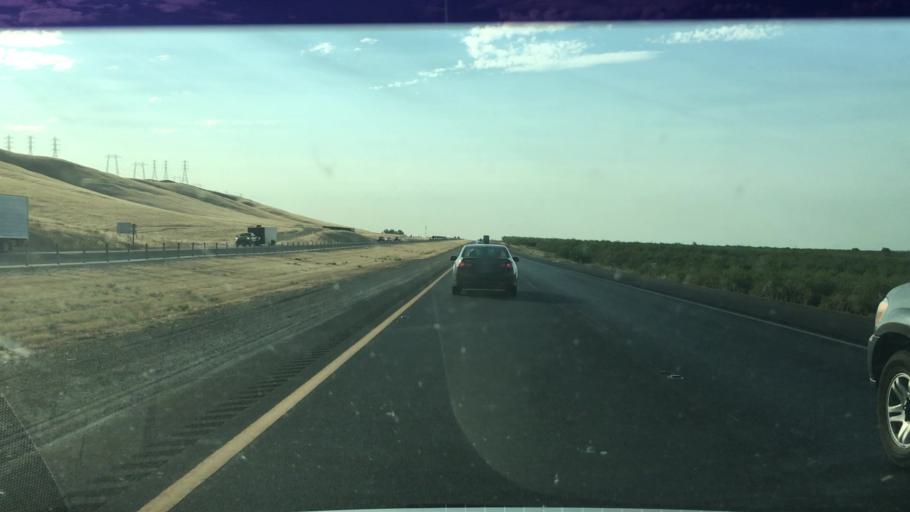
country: US
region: California
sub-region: Stanislaus County
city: Patterson
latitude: 37.5526
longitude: -121.2836
